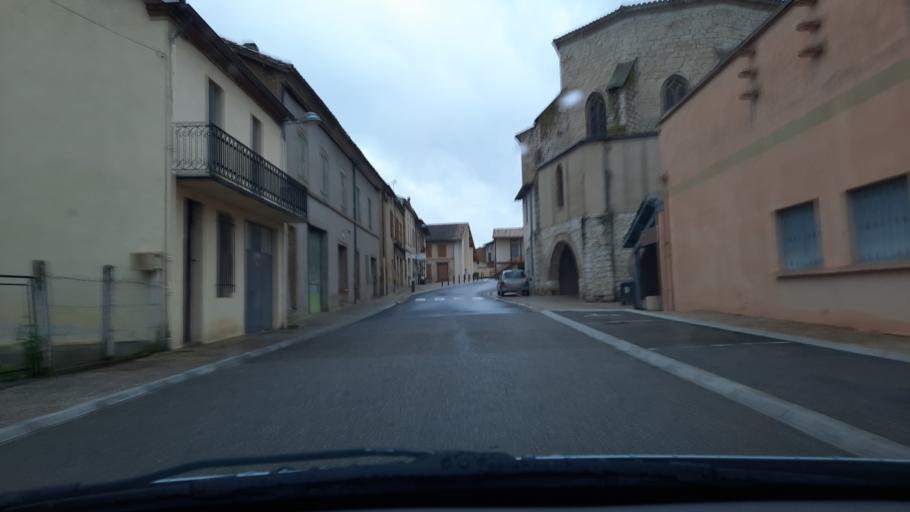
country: FR
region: Midi-Pyrenees
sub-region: Departement du Tarn-et-Garonne
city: Lafrancaise
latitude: 44.1903
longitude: 1.2862
